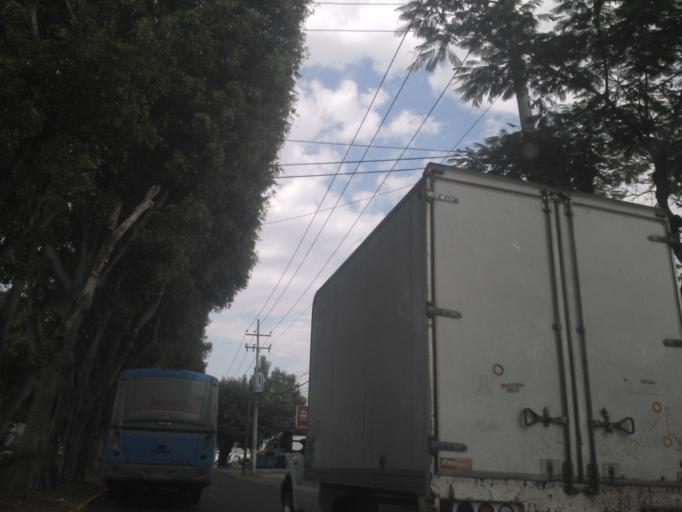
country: MX
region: Jalisco
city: Guadalajara
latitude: 20.6613
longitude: -103.3804
